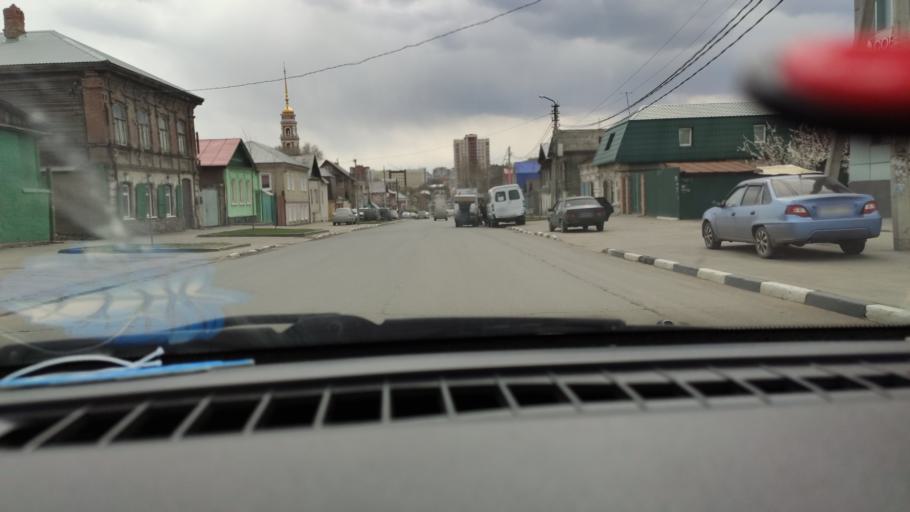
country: RU
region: Saratov
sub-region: Saratovskiy Rayon
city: Saratov
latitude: 51.5413
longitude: 46.0352
